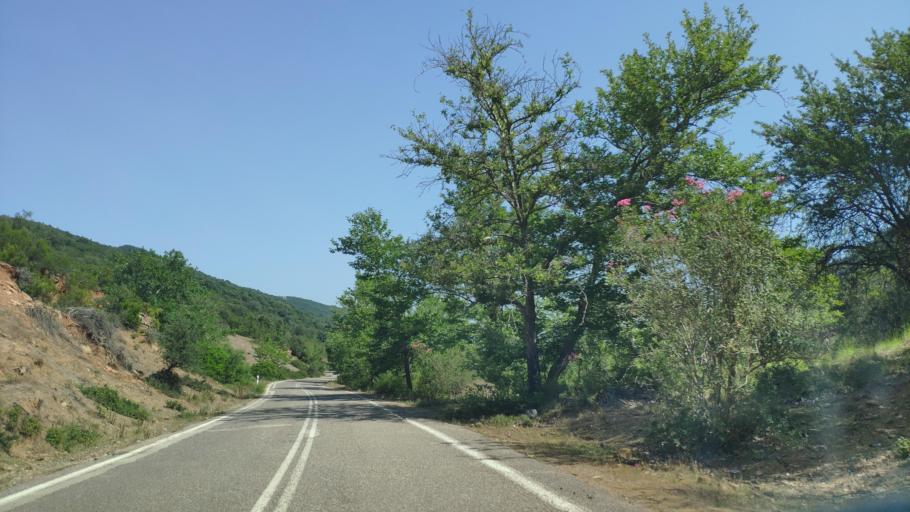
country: GR
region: West Greece
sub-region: Nomos Aitolias kai Akarnanias
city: Lepenou
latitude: 38.7878
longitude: 21.3341
